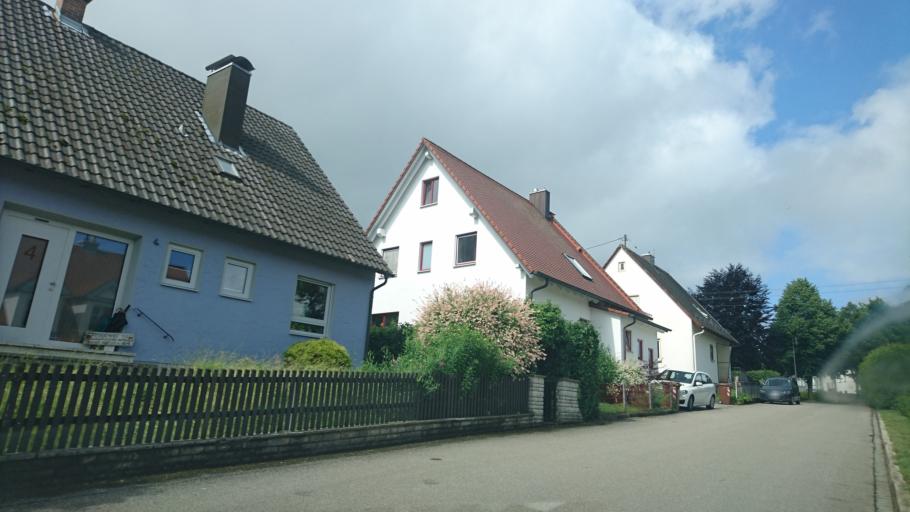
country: DE
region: Bavaria
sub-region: Swabia
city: Zusmarshausen
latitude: 48.3961
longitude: 10.5999
